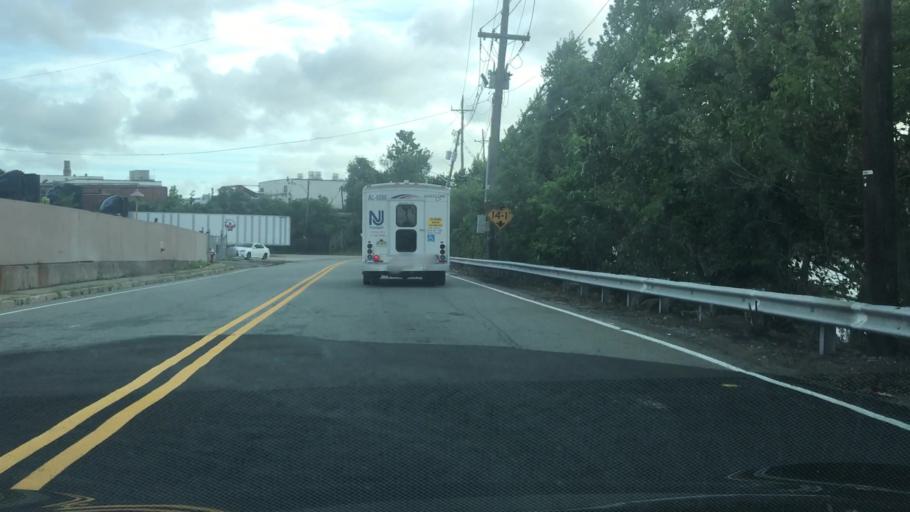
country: US
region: New Jersey
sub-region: Bergen County
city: Elmwood Park
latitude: 40.9051
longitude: -74.1311
